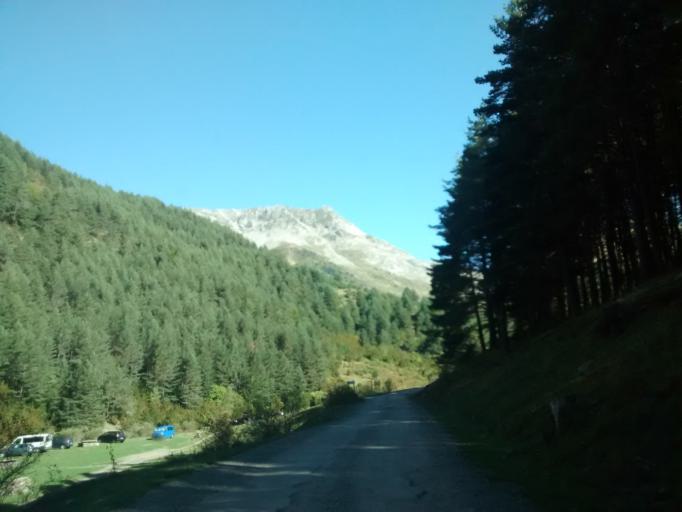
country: ES
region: Aragon
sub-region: Provincia de Huesca
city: Aragues del Puerto
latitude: 42.8500
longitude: -0.7042
